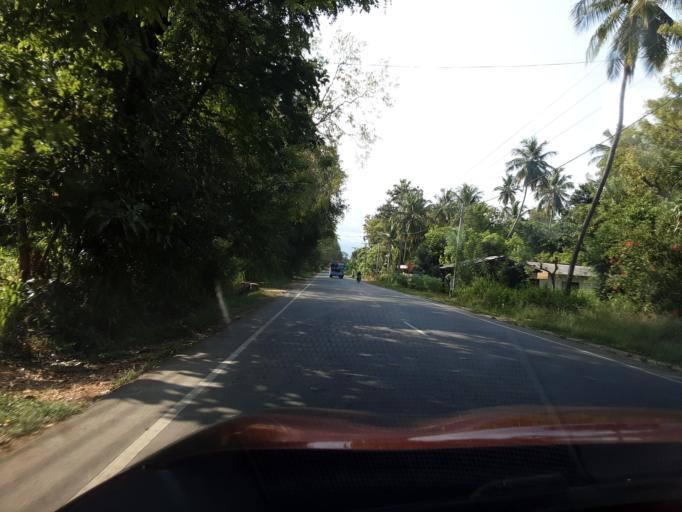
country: LK
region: Uva
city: Haputale
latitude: 6.6164
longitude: 81.1290
